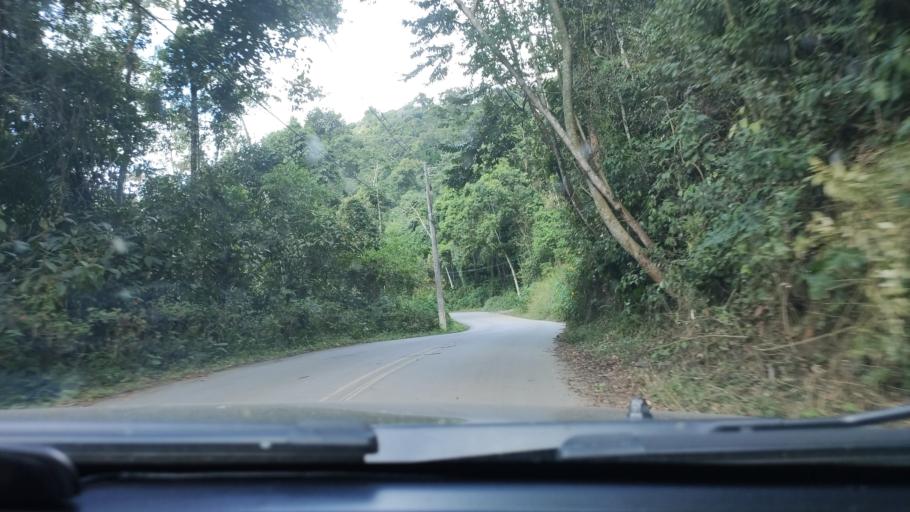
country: BR
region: Sao Paulo
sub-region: Sao Sebastiao
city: Sao Sebastiao
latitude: -23.7007
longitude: -45.4780
